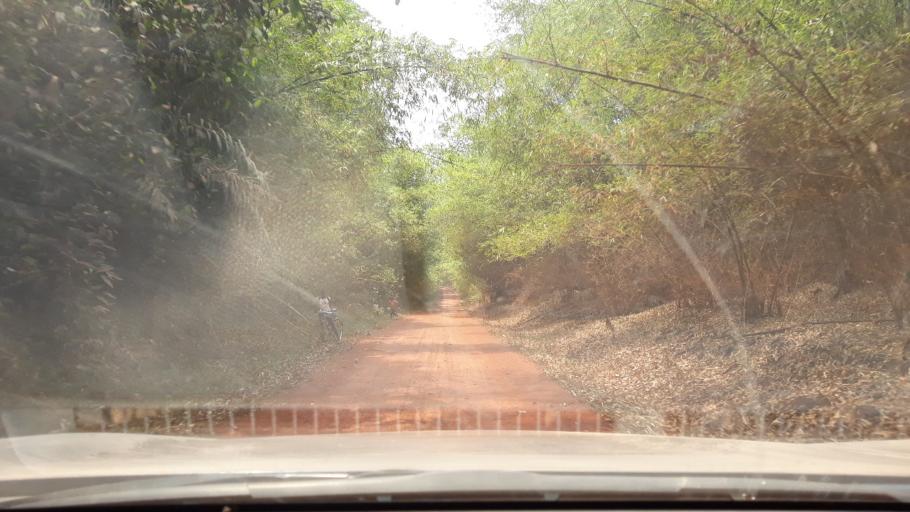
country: CD
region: Eastern Province
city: Buta
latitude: 2.3011
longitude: 25.0289
